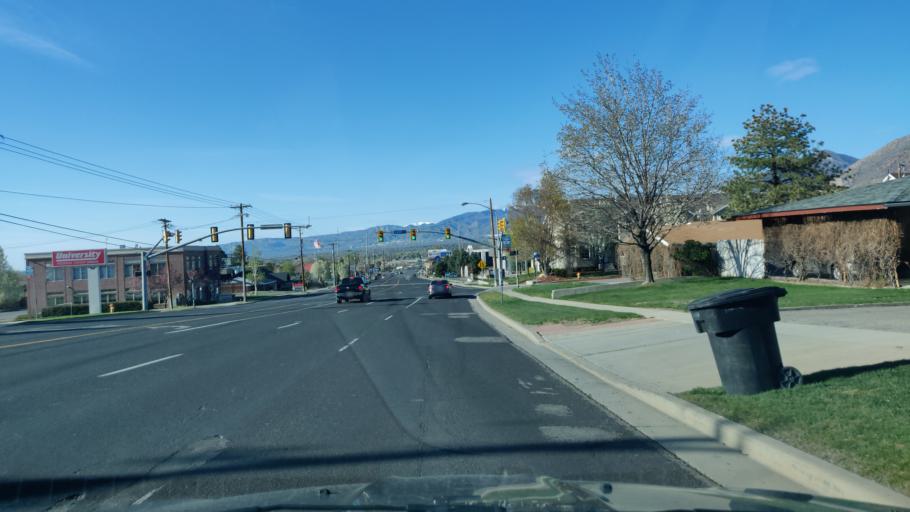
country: US
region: Utah
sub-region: Salt Lake County
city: Little Cottonwood Creek Valley
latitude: 40.6197
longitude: -111.8343
